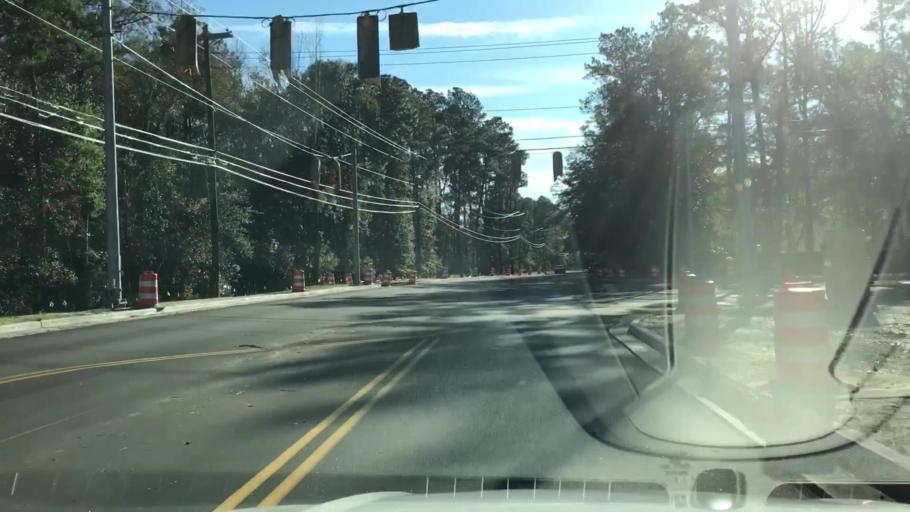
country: US
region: South Carolina
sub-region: Charleston County
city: Lincolnville
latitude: 32.9837
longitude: -80.1423
